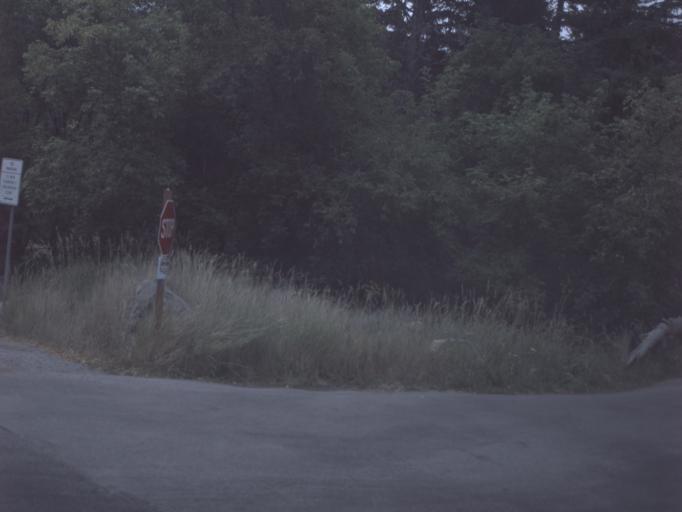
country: US
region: Utah
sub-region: Utah County
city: Lindon
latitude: 40.3932
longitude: -111.5814
